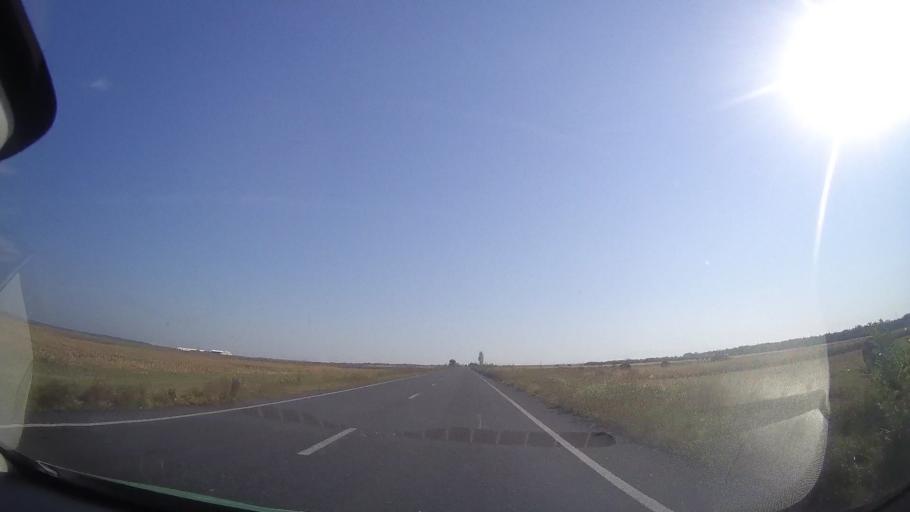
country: RO
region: Timis
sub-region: Comuna Topolovatu Mare
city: Topolovatu Mare
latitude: 45.7749
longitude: 21.6410
